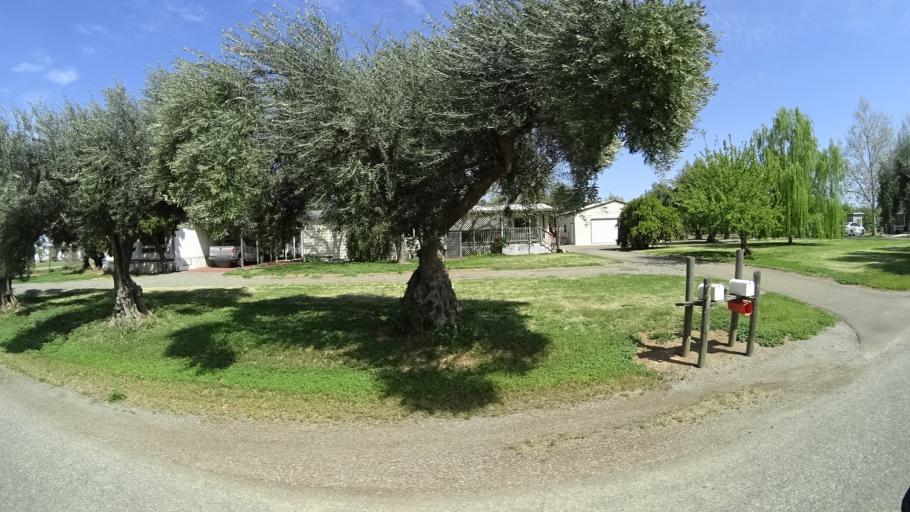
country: US
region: California
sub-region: Glenn County
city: Hamilton City
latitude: 39.8042
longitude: -122.0943
